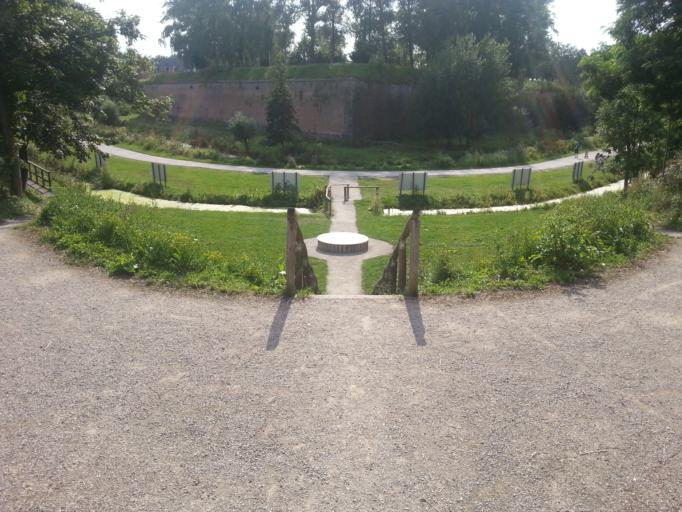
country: FR
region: Nord-Pas-de-Calais
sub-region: Departement du Nord
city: Lille
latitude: 50.6420
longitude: 3.0492
